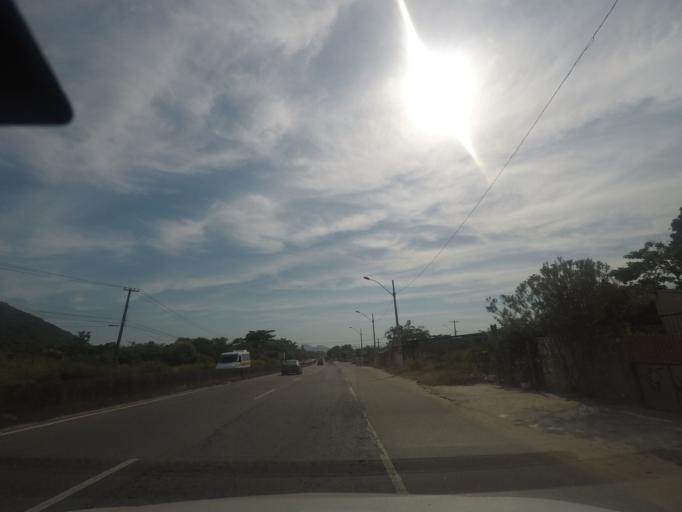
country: BR
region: Rio de Janeiro
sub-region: Marica
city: Marica
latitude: -22.9353
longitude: -42.9017
